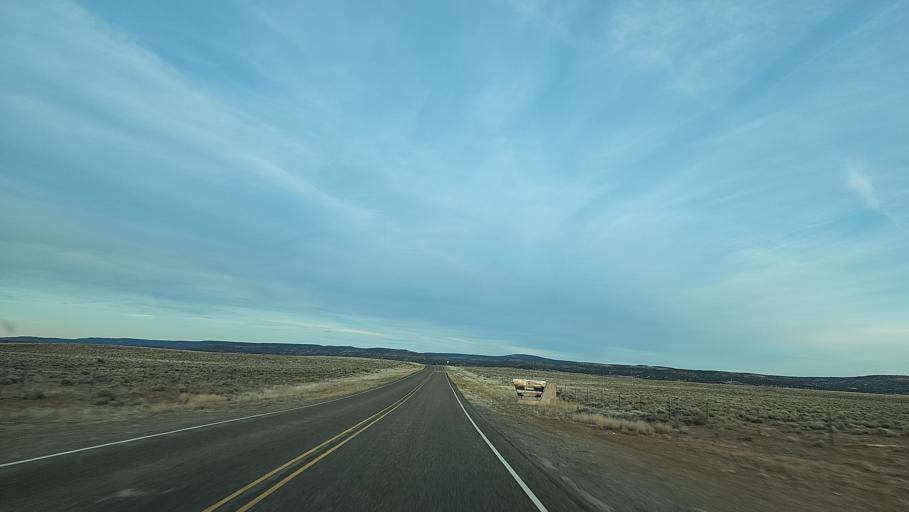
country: US
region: New Mexico
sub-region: Cibola County
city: Grants
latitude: 34.6980
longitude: -108.0452
